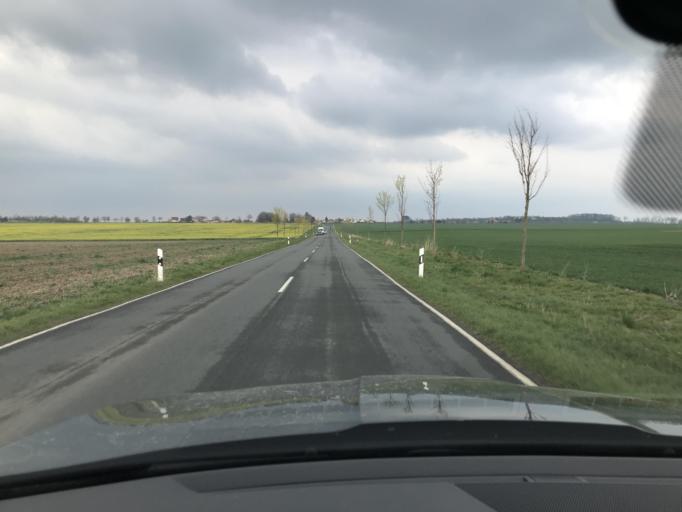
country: DE
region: Saxony-Anhalt
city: Ballenstedt
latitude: 51.7507
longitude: 11.2384
